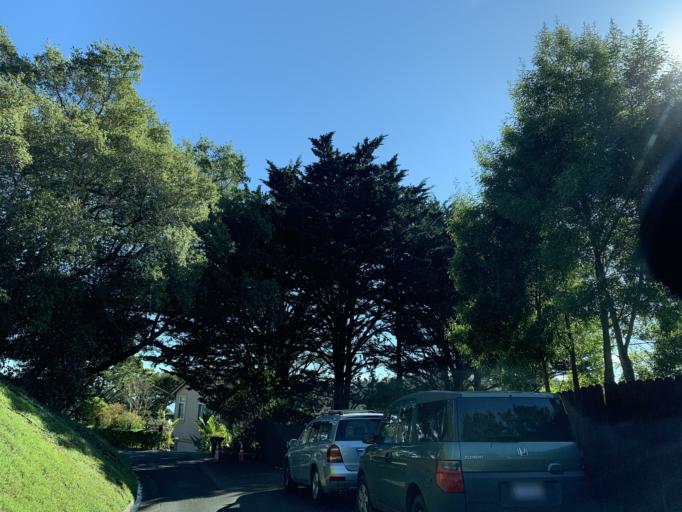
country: US
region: California
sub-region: Marin County
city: Strawberry
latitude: 37.9036
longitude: -122.5123
